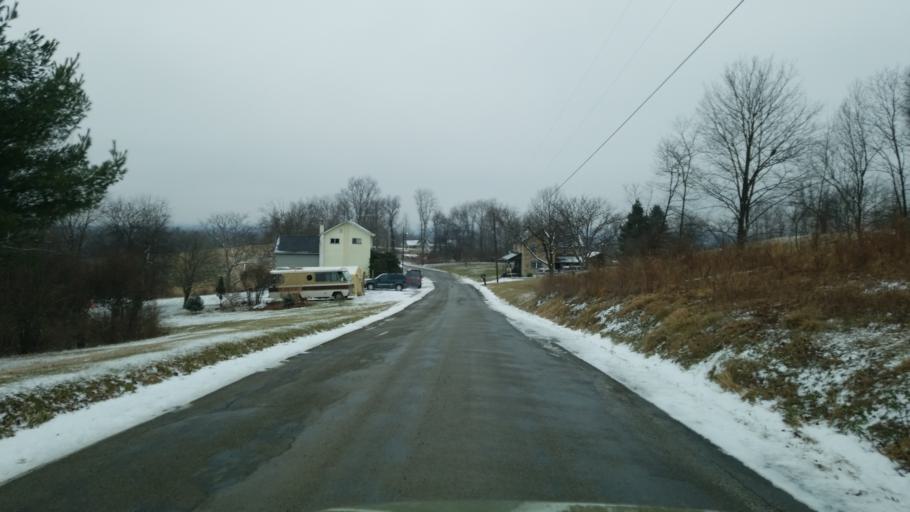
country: US
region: Pennsylvania
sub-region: Jefferson County
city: Sykesville
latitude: 41.0848
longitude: -78.8397
